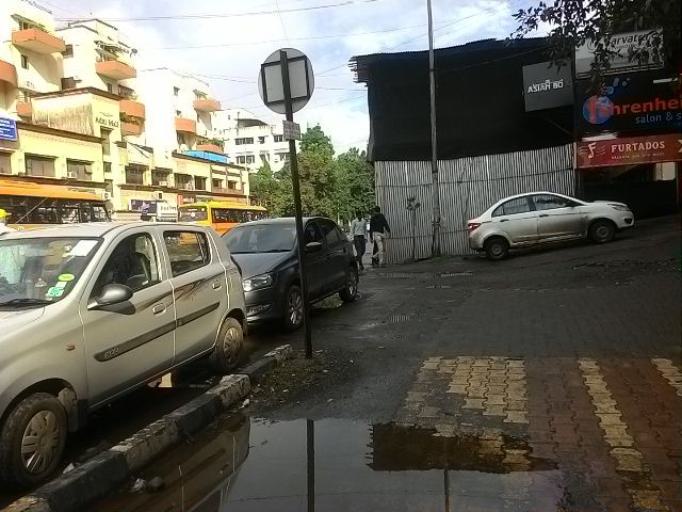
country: IN
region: Maharashtra
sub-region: Pune Division
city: Khadki
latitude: 18.5583
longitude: 73.7922
